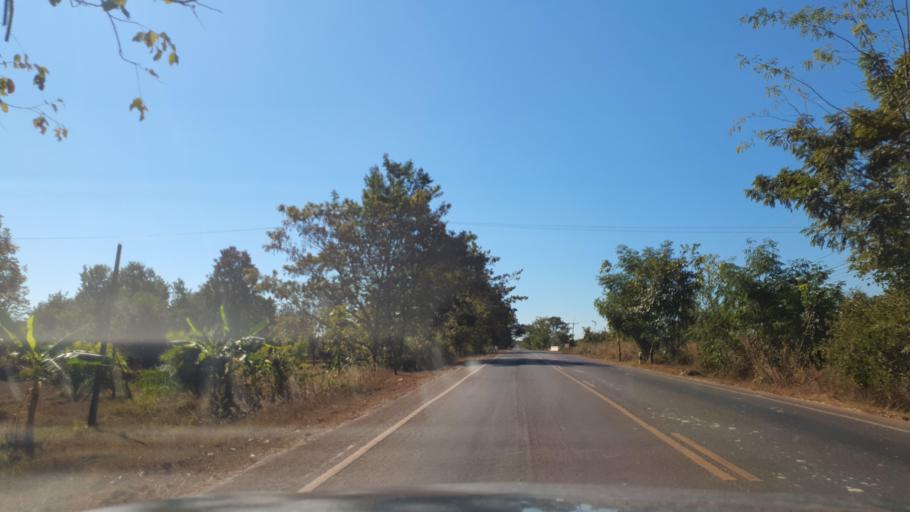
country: TH
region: Nakhon Phanom
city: Si Songkhram
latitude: 17.7506
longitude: 104.2862
